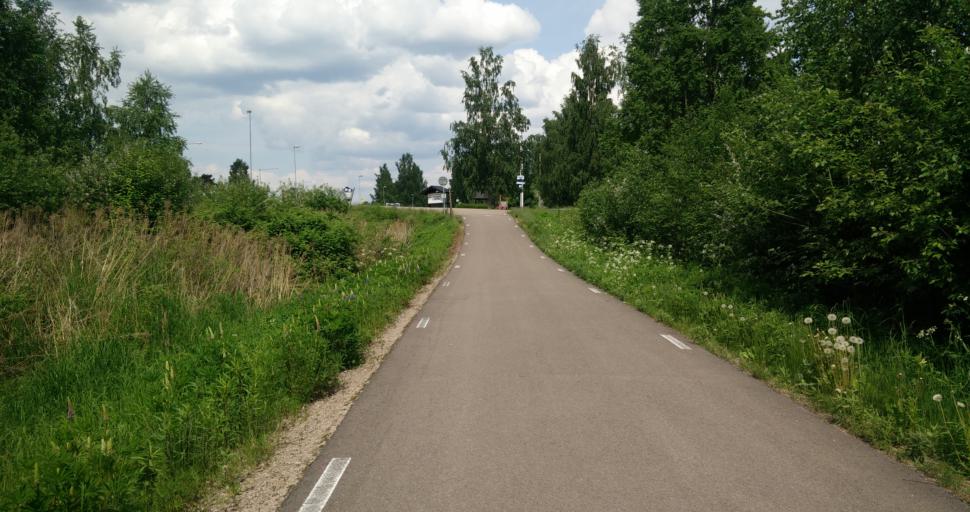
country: SE
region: Vaermland
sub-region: Hagfors Kommun
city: Hagfors
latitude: 60.0029
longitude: 13.6052
